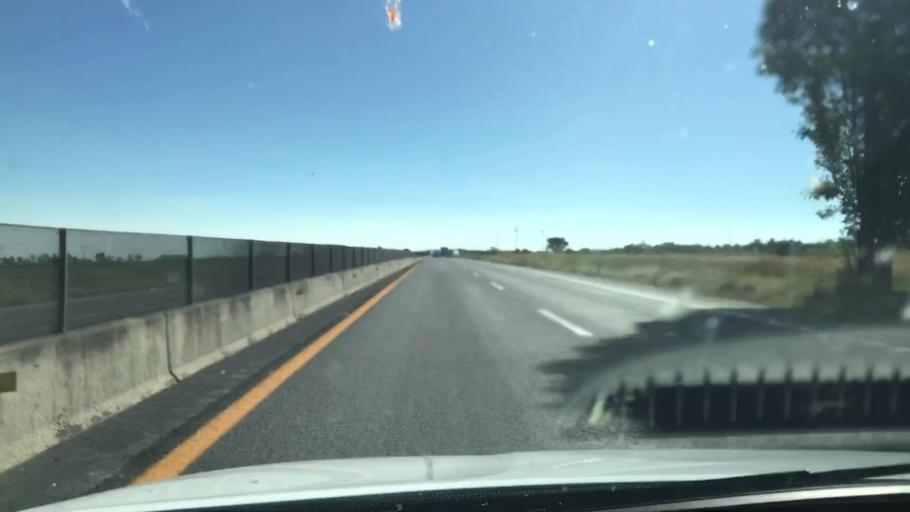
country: MX
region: Jalisco
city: Valle de Guadalupe
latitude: 20.9206
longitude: -102.6709
